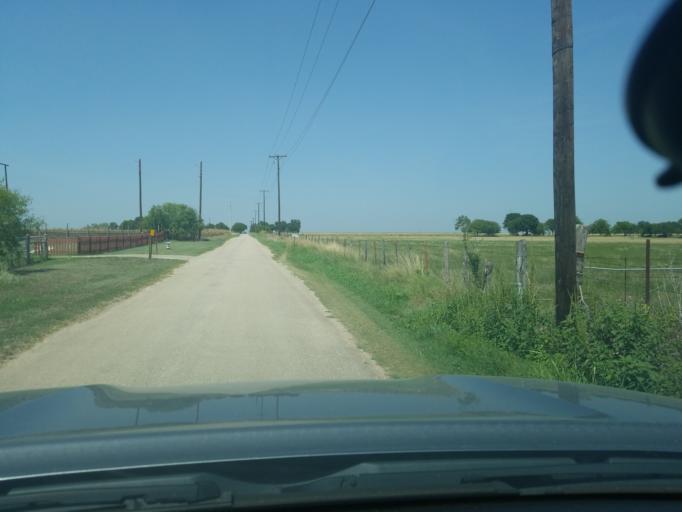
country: US
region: Texas
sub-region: Guadalupe County
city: Lake Dunlap
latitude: 29.6743
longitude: -98.0499
